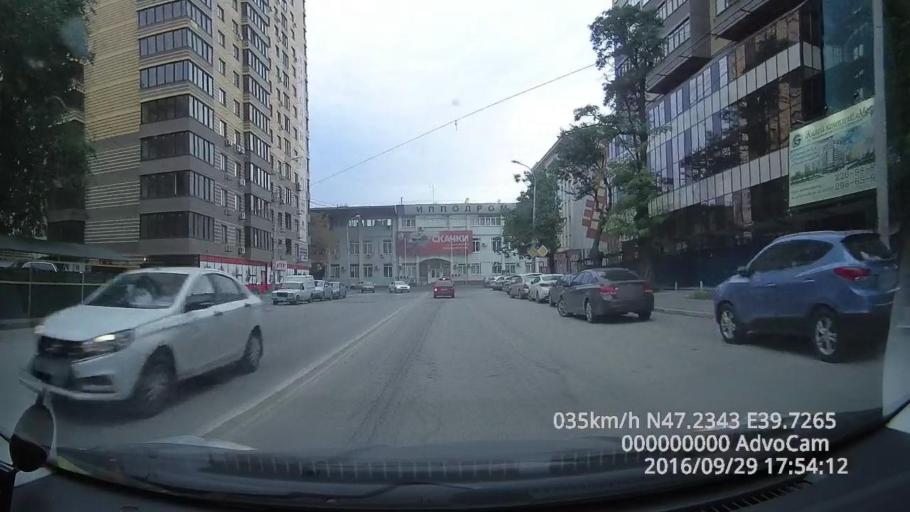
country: RU
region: Rostov
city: Rostov-na-Donu
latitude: 47.2346
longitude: 39.7263
